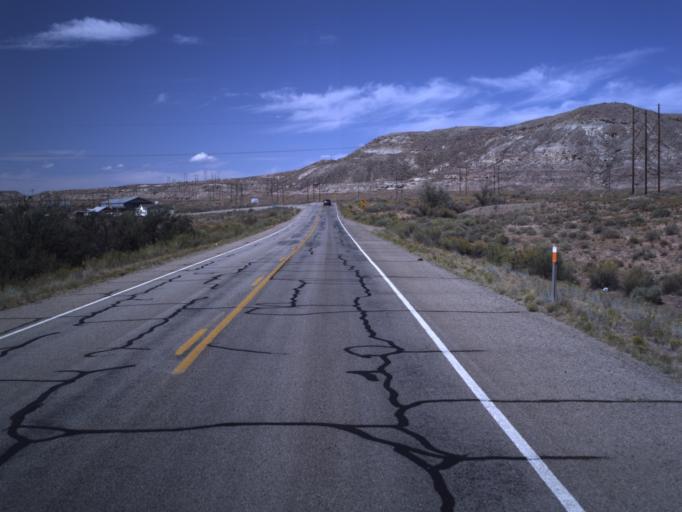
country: US
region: Utah
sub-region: San Juan County
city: Blanding
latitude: 37.2727
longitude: -109.3296
